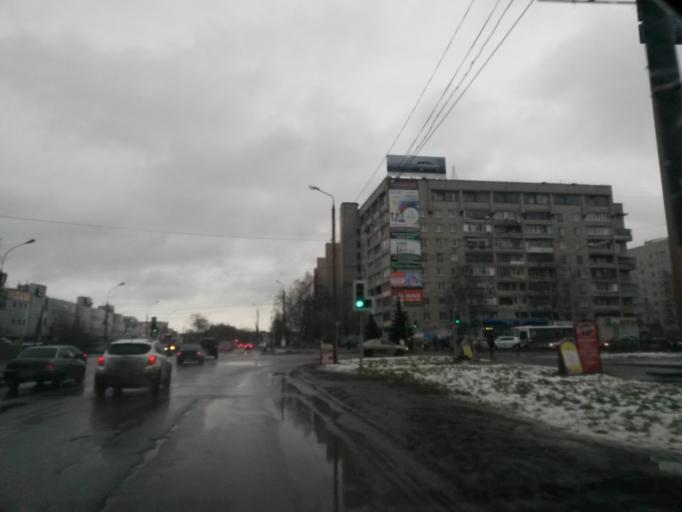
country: RU
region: Jaroslavl
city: Yaroslavl
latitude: 57.6543
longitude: 39.9417
